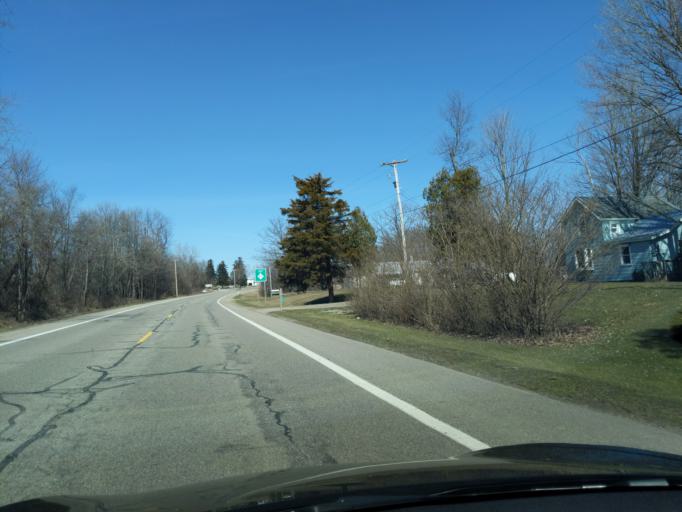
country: US
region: Michigan
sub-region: Ionia County
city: Lake Odessa
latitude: 42.7232
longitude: -85.0948
